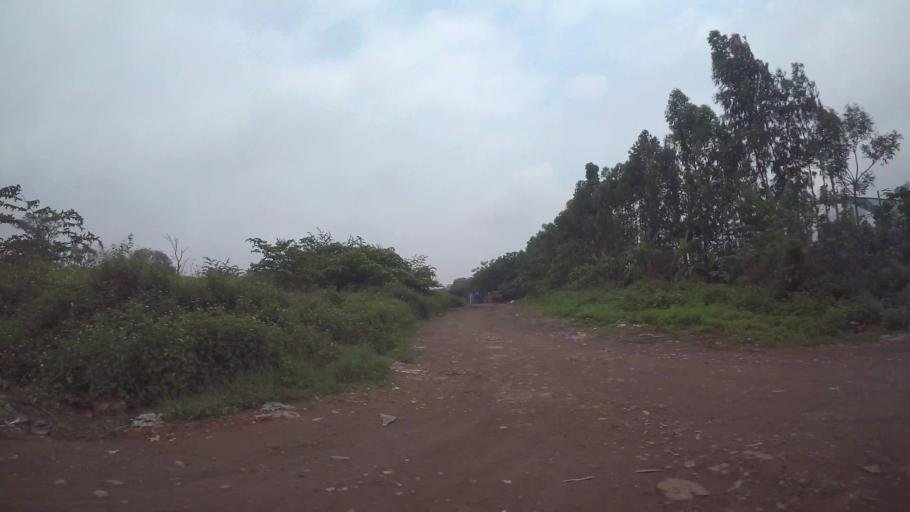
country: VN
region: Ha Noi
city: Van Dien
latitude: 20.9757
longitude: 105.8602
